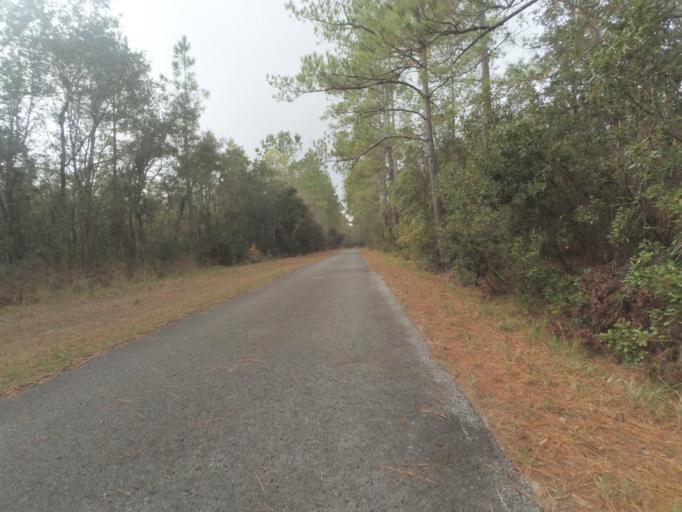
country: US
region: Florida
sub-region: Alachua County
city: Gainesville
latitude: 29.6126
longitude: -82.2645
